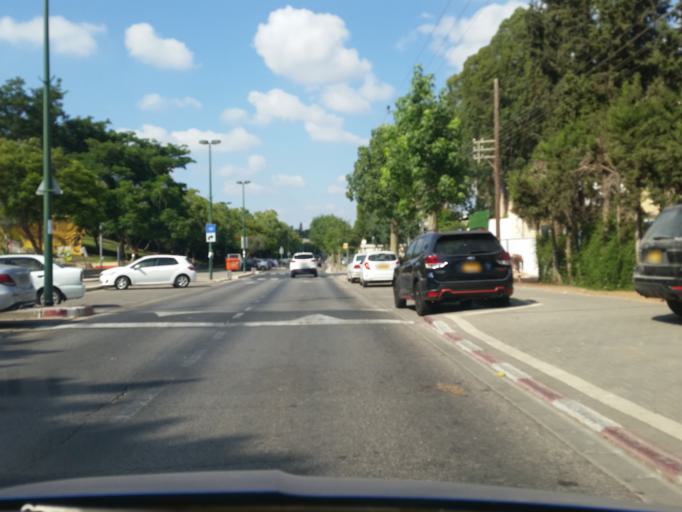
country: IL
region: Tel Aviv
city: Ramat HaSharon
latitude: 32.1164
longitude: 34.8337
